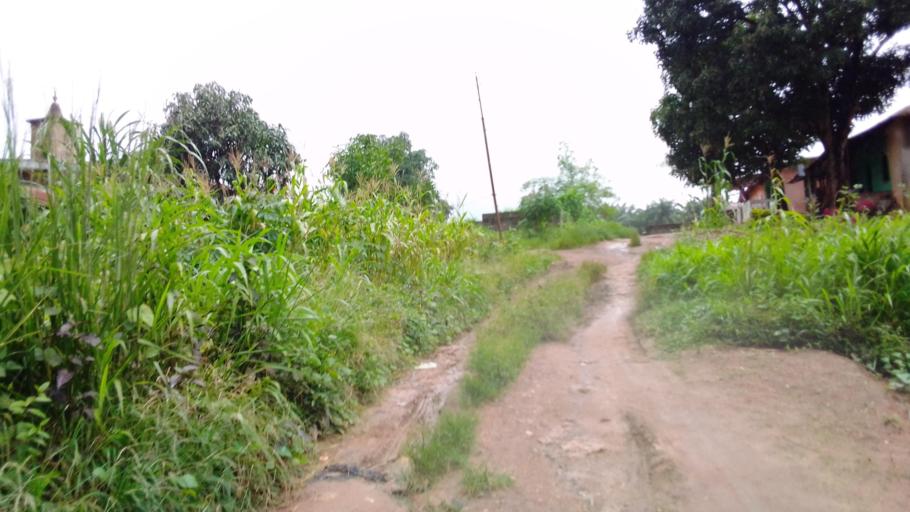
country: SL
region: Eastern Province
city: Kenema
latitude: 7.8756
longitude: -11.1706
